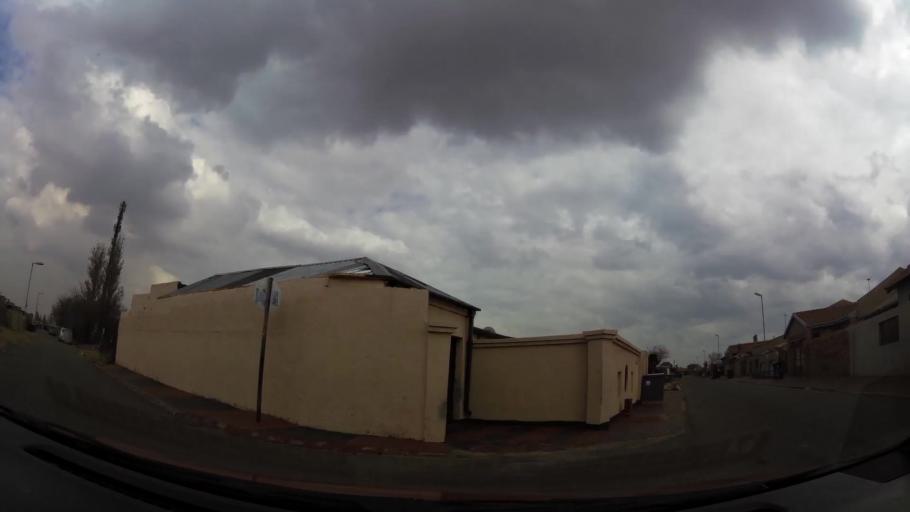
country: ZA
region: Gauteng
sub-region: City of Johannesburg Metropolitan Municipality
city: Soweto
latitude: -26.2511
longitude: 27.8349
